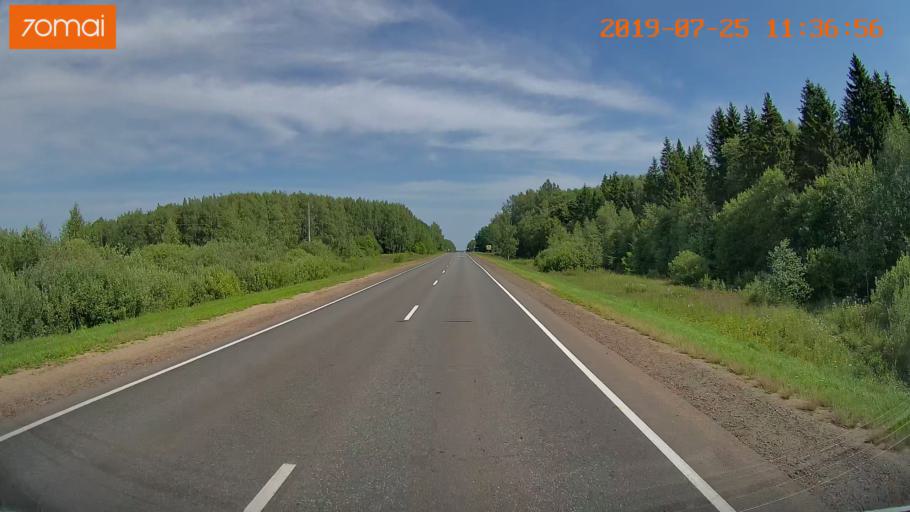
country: RU
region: Ivanovo
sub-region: Privolzhskiy Rayon
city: Ples
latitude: 57.4282
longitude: 41.4586
